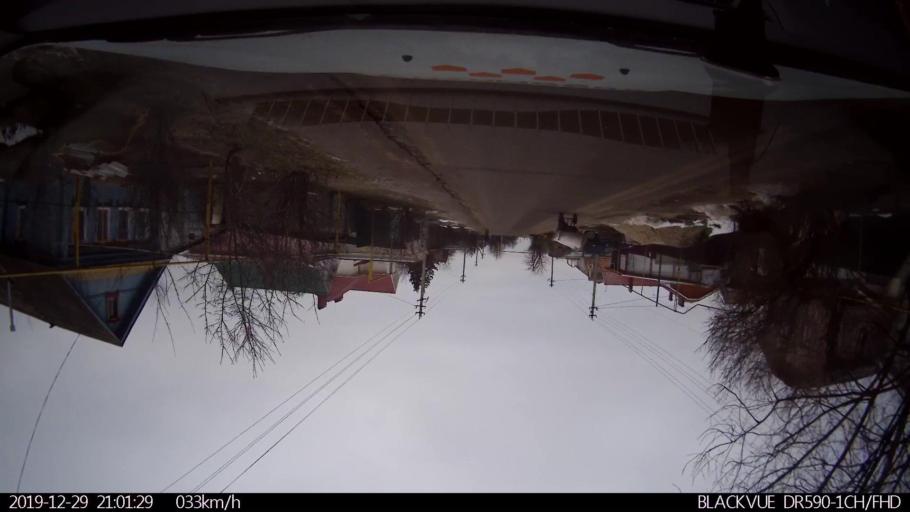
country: RU
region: Nizjnij Novgorod
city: Afonino
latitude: 56.1879
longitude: 43.9907
